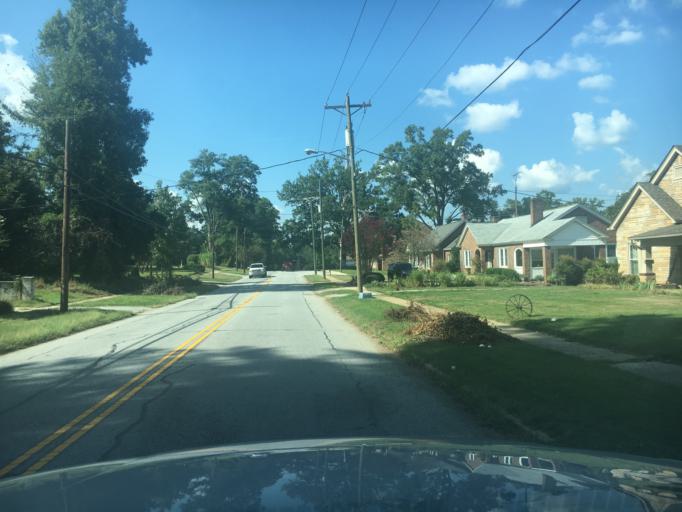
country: US
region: South Carolina
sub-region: Greenwood County
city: Greenwood
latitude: 34.2040
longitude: -82.1624
